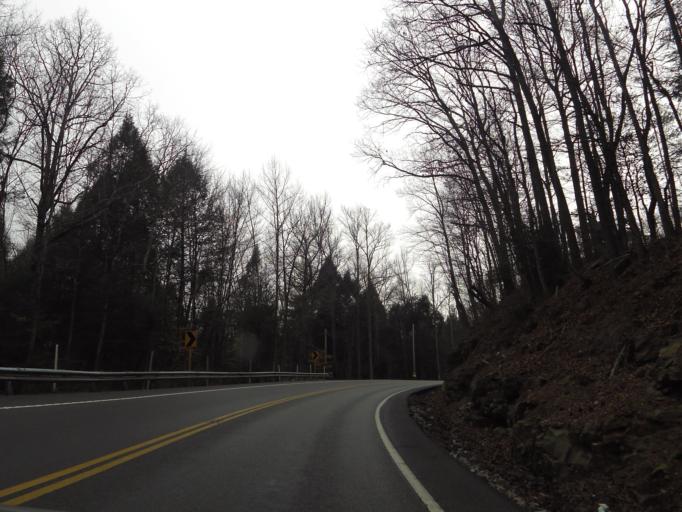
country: US
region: Tennessee
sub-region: Morgan County
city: Wartburg
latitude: 36.0429
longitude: -84.5278
